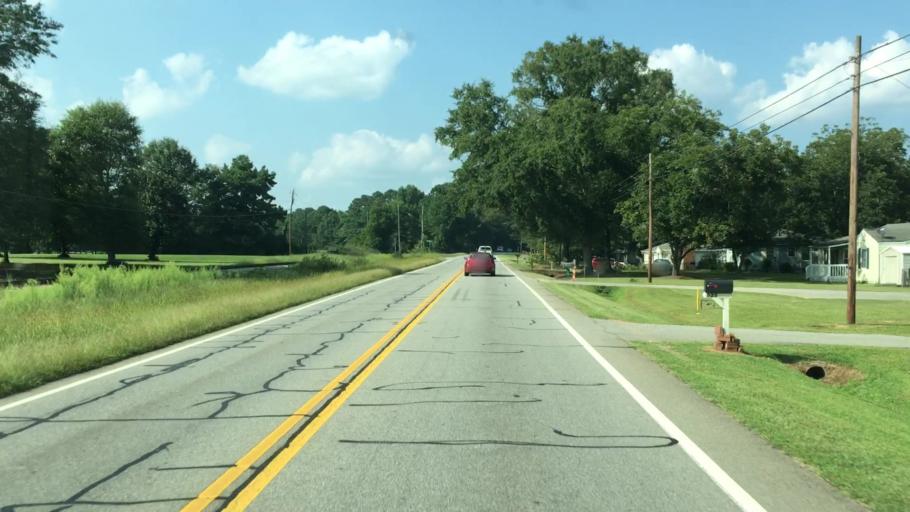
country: US
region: Georgia
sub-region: Walton County
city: Monroe
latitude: 33.7502
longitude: -83.7021
